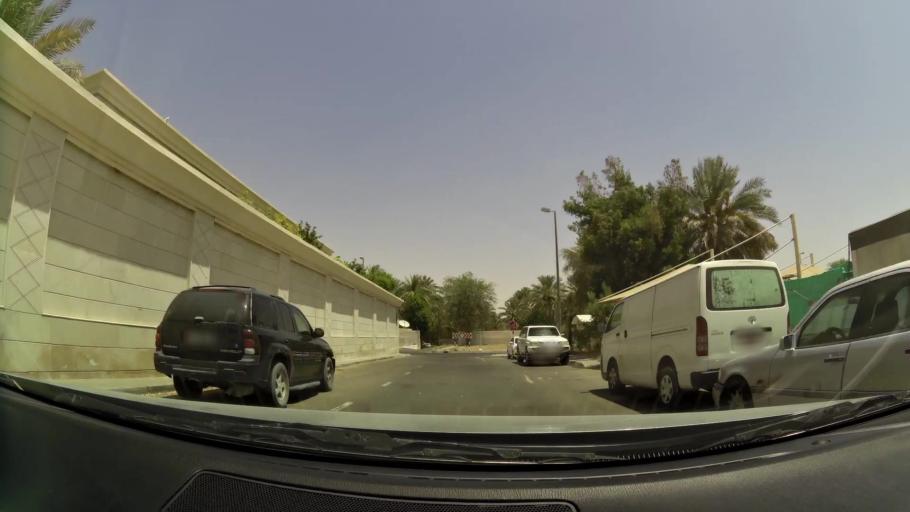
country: OM
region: Al Buraimi
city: Al Buraymi
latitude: 24.2739
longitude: 55.7430
